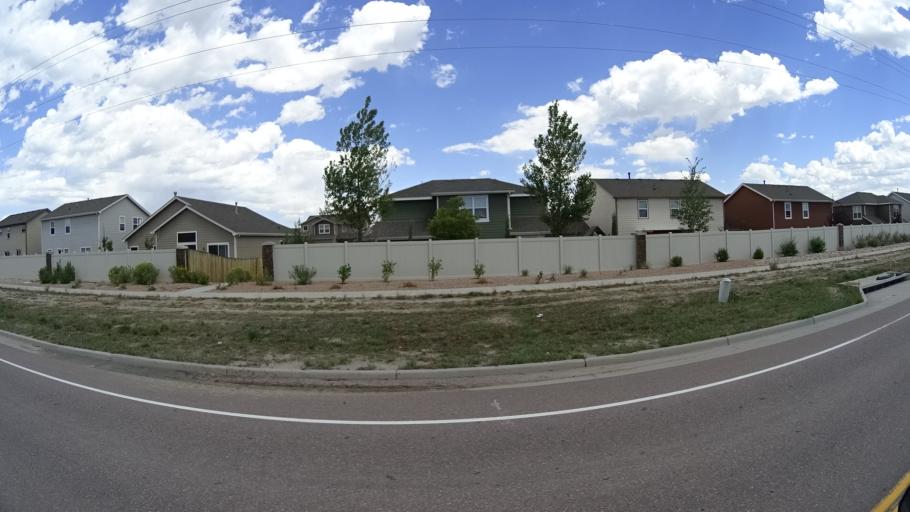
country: US
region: Colorado
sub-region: El Paso County
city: Black Forest
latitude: 38.9450
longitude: -104.7010
